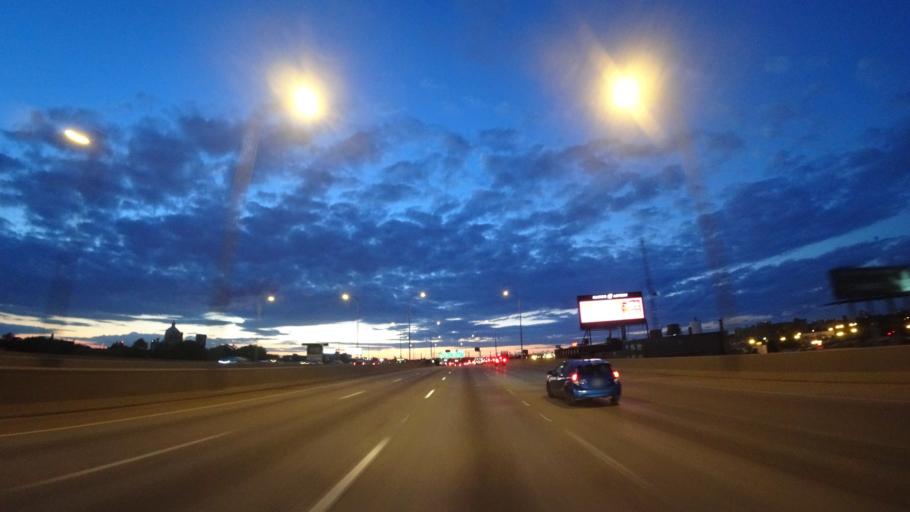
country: US
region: Illinois
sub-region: Cook County
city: Chicago
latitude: 41.9139
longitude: -87.6668
